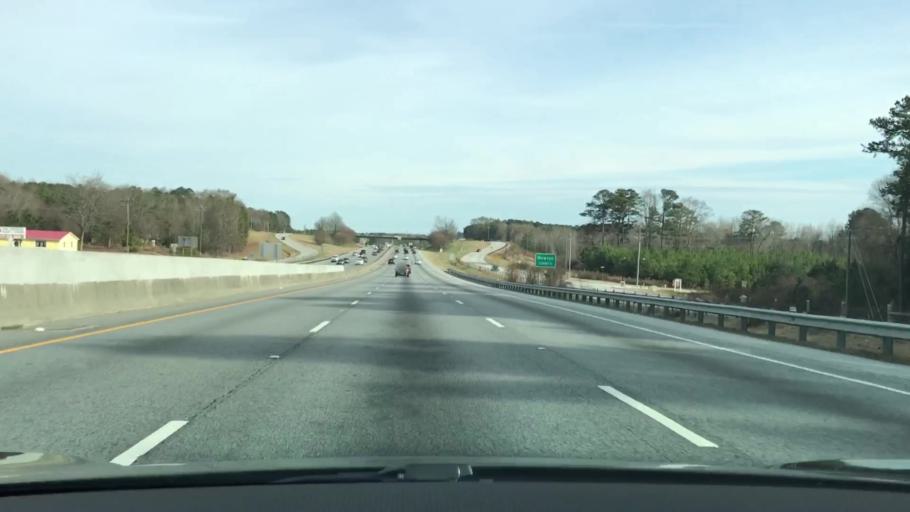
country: US
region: Georgia
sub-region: Rockdale County
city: Conyers
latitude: 33.6291
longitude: -83.9539
